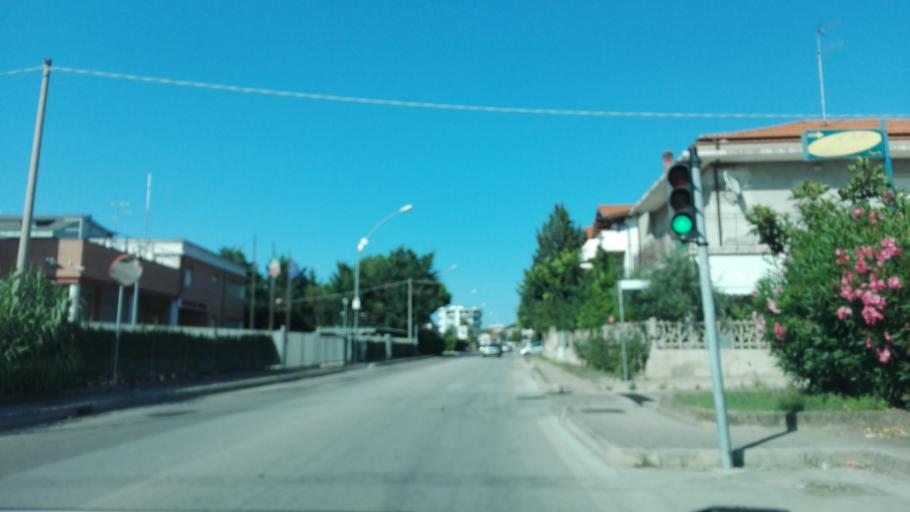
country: IT
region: Abruzzo
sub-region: Provincia di Pescara
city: Montesilvano Marina
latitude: 42.5038
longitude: 14.1407
